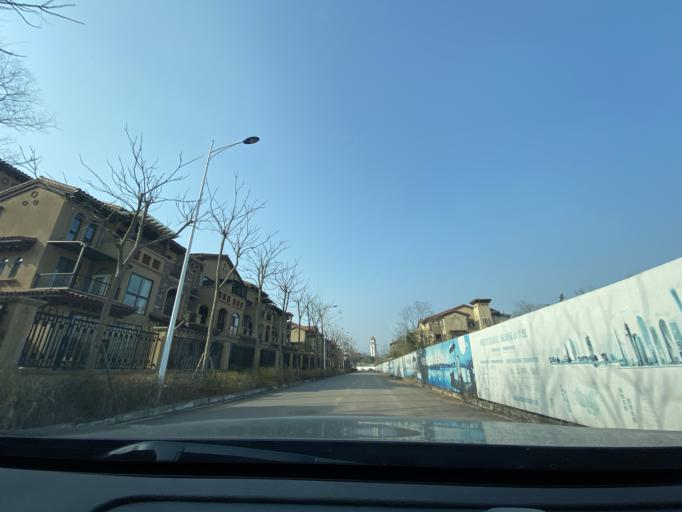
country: CN
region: Sichuan
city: Wenlin
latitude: 30.2532
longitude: 104.2458
